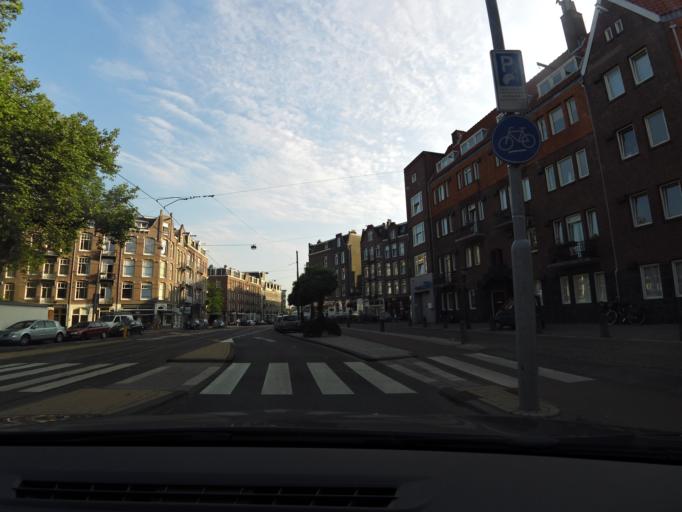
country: NL
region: North Holland
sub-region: Gemeente Amsterdam
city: Amsterdam
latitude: 52.3507
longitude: 4.8917
